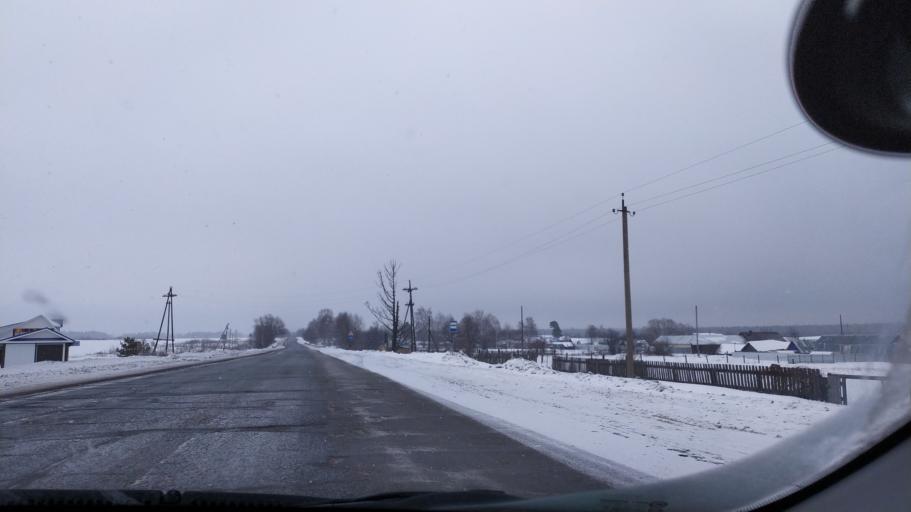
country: RU
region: Mariy-El
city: Krasnogorskiy
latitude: 56.1485
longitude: 48.1355
